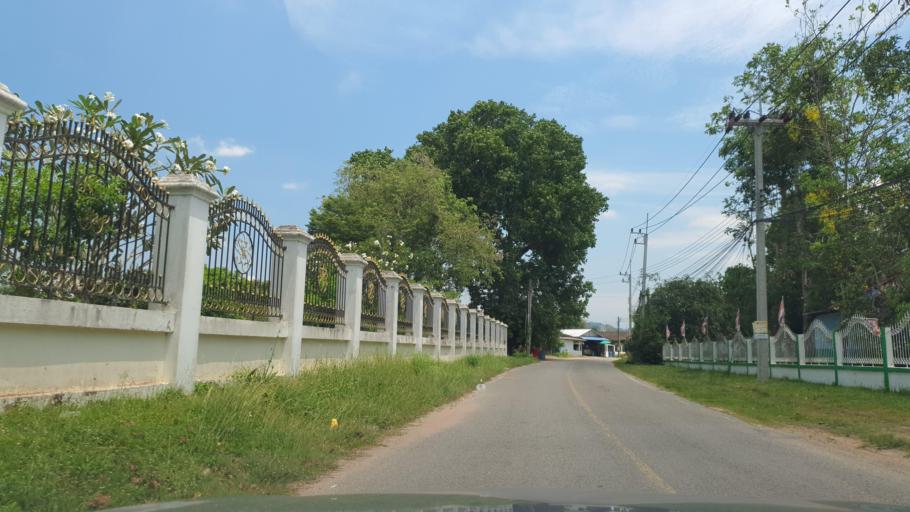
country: TH
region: Rayong
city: Ban Chang
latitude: 12.8060
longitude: 100.9483
